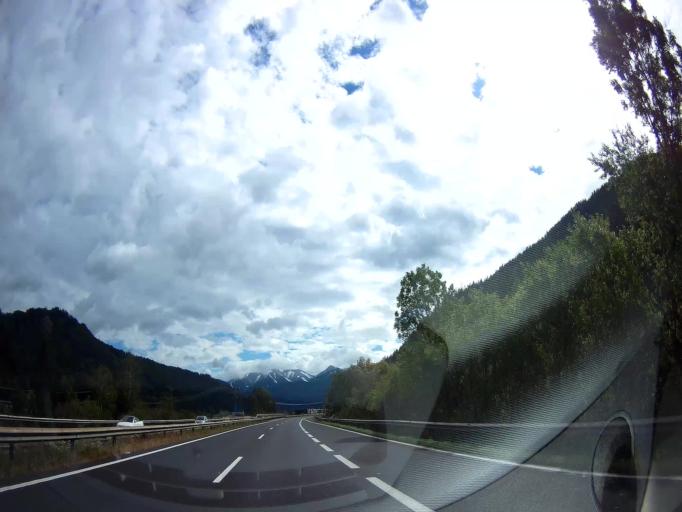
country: AT
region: Styria
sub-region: Politischer Bezirk Leoben
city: Traboch
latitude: 47.3651
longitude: 14.9942
